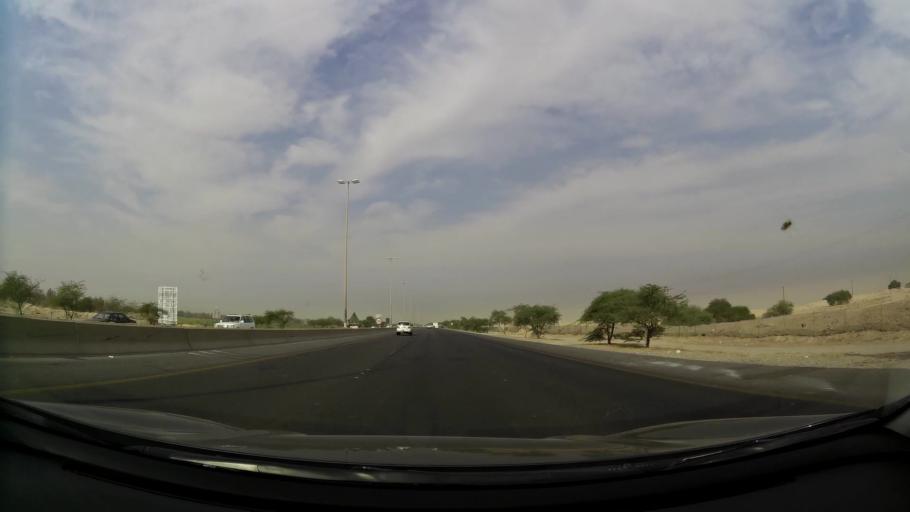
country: KW
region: Muhafazat al Jahra'
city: Al Jahra'
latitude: 29.2866
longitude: 47.7758
